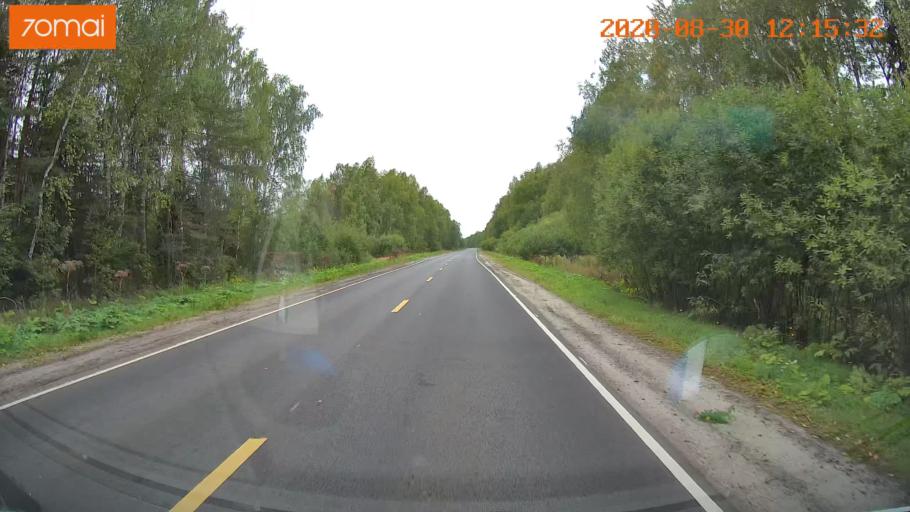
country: RU
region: Ivanovo
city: Yur'yevets
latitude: 57.3176
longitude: 43.0272
